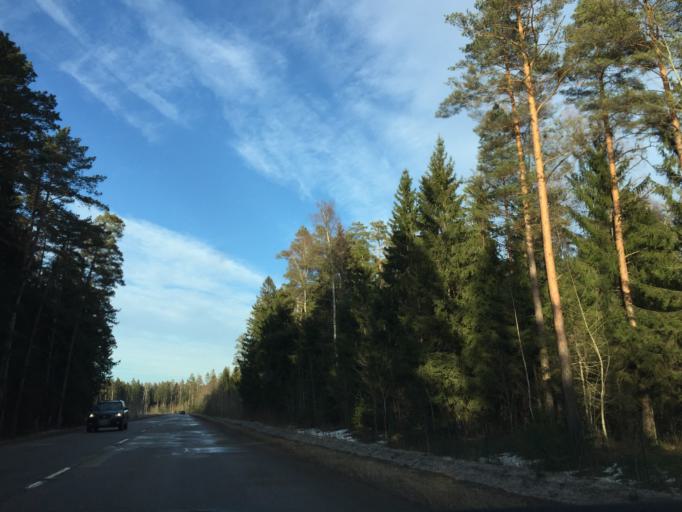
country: LV
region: Kekava
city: Balozi
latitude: 56.7531
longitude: 24.1083
